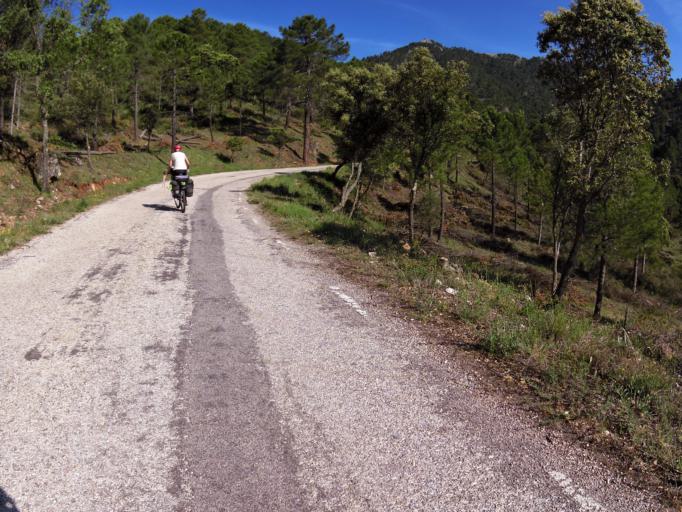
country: ES
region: Castille-La Mancha
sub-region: Provincia de Albacete
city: Riopar
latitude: 38.5194
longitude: -2.4545
